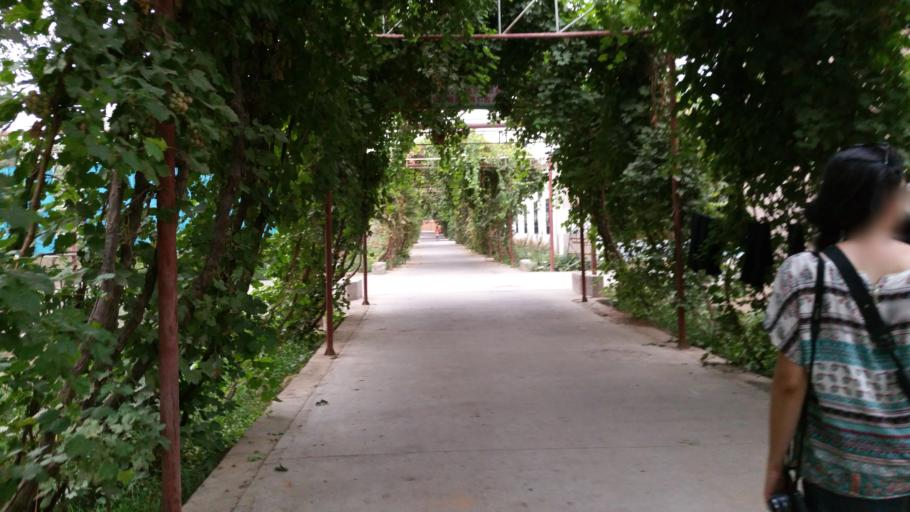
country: CN
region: Xinjiang Uygur Zizhiqu
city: Laochenglu
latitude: 42.9469
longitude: 89.1951
